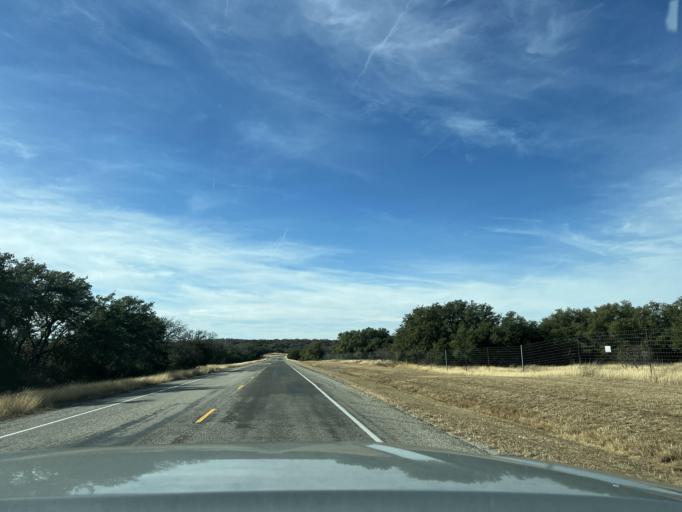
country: US
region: Texas
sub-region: Eastland County
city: Cisco
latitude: 32.4604
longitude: -99.0055
